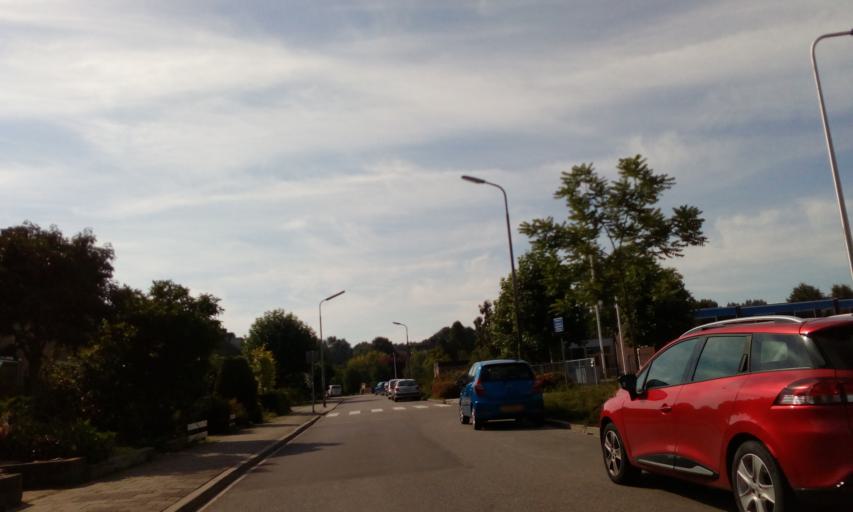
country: NL
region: South Holland
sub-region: Gemeente Boskoop
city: Boskoop
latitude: 52.0665
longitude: 4.6441
